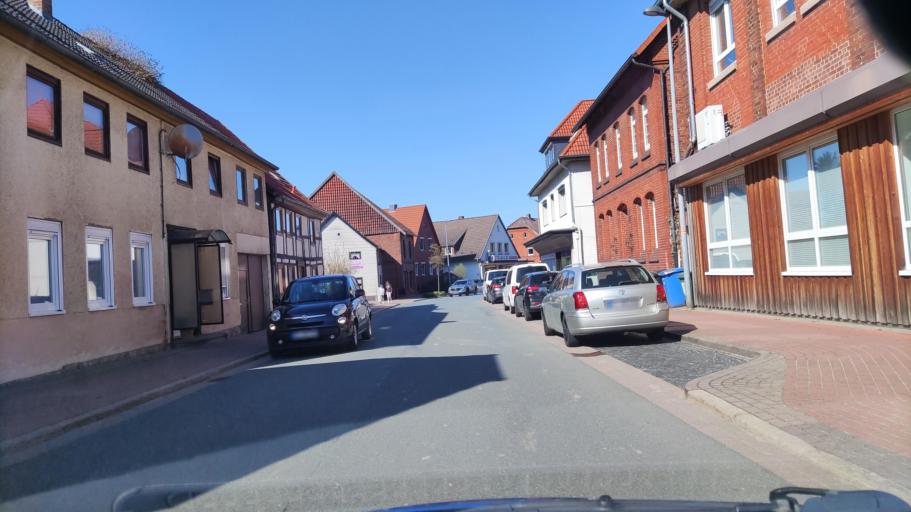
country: DE
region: Lower Saxony
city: Nordstemmen
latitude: 52.1625
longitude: 9.7835
